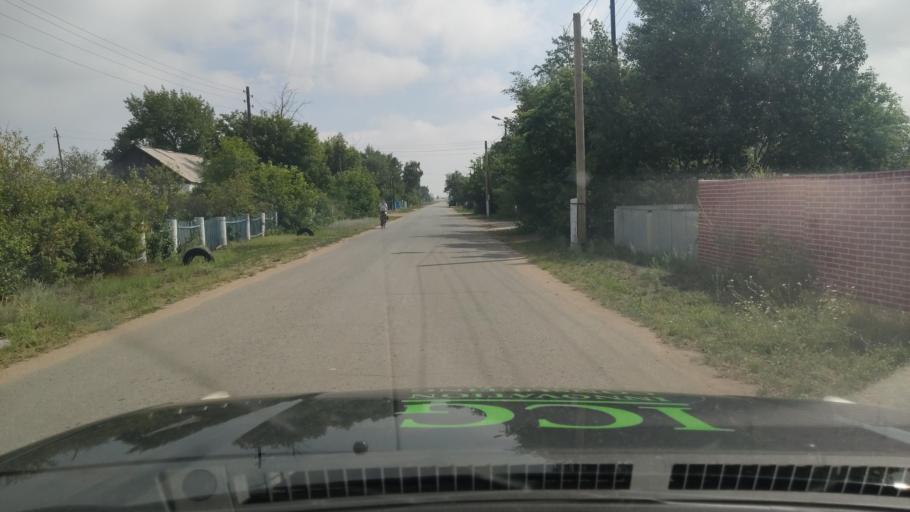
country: KZ
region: Pavlodar
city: Koktobe
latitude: 51.9654
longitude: 77.6378
